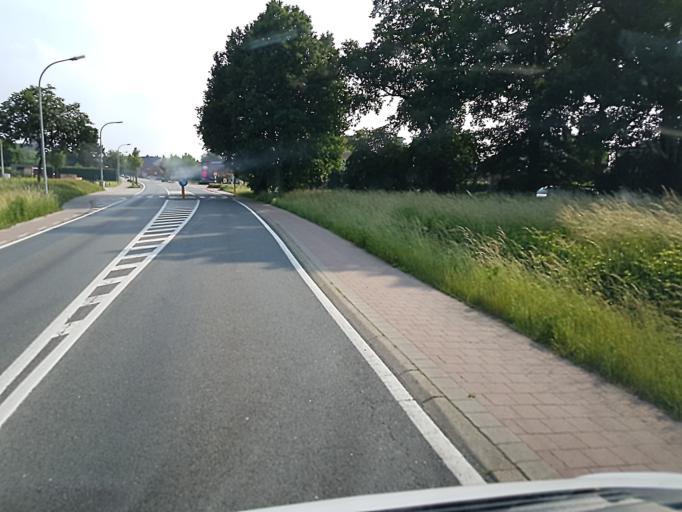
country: BE
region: Flanders
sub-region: Provincie Antwerpen
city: Merksplas
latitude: 51.3631
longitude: 4.8644
